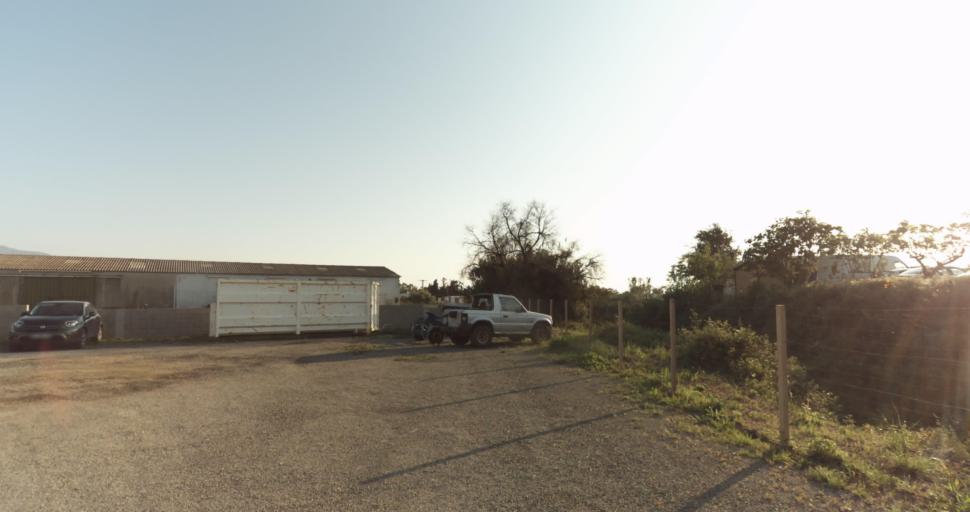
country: FR
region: Corsica
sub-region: Departement de la Haute-Corse
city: Biguglia
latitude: 42.5984
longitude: 9.4410
